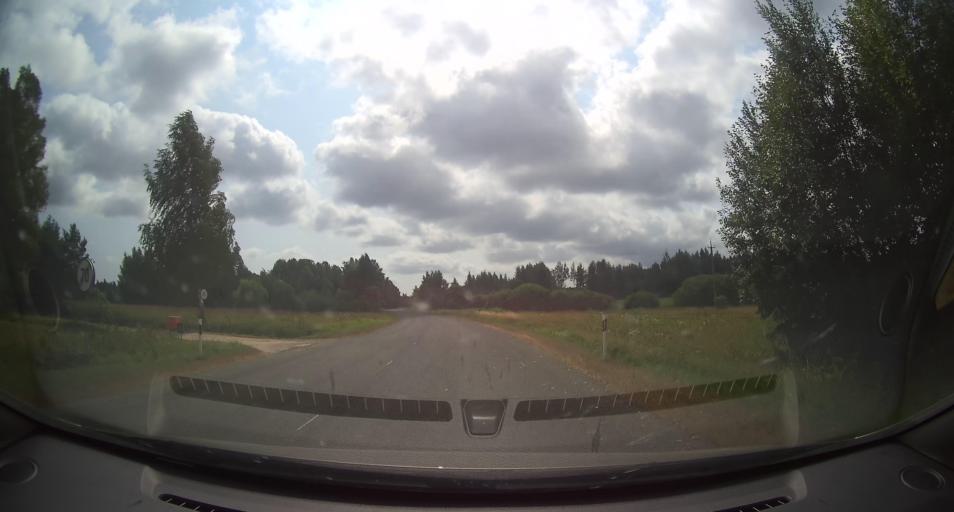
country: EE
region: Paernumaa
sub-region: Audru vald
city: Audru
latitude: 58.4424
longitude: 24.3069
